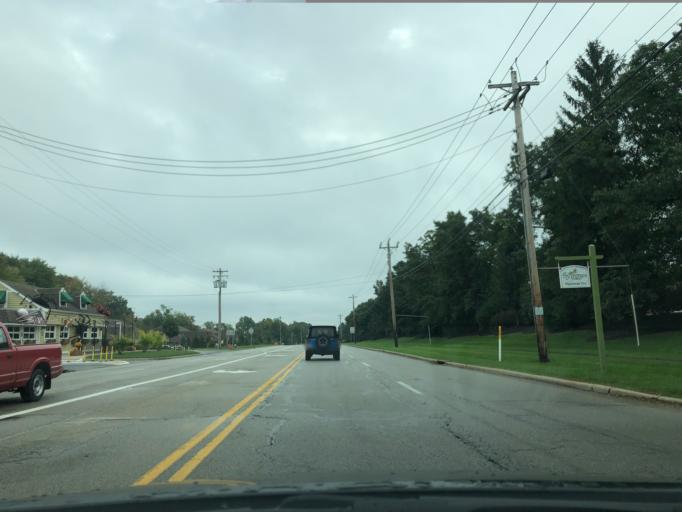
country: US
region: Ohio
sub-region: Hamilton County
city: Sixteen Mile Stand
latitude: 39.2759
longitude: -84.3359
